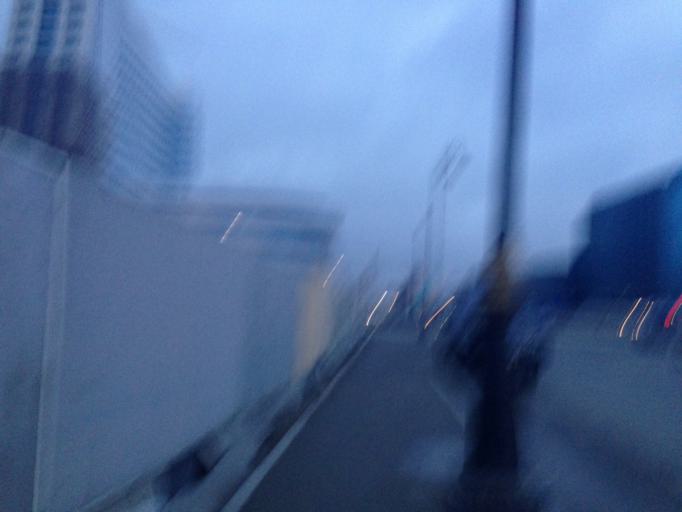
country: AZ
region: Baki
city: Baku
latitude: 40.4129
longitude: 49.8976
